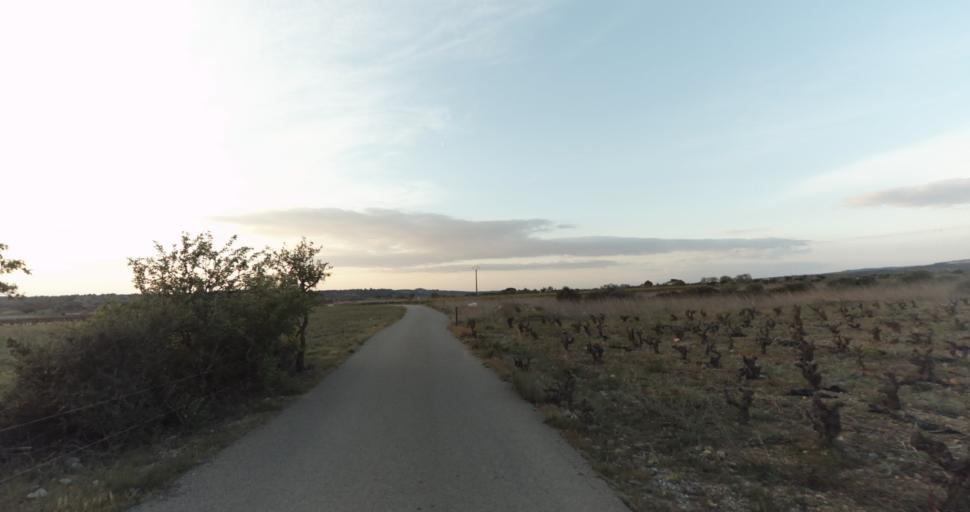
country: FR
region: Languedoc-Roussillon
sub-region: Departement de l'Aude
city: Leucate
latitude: 42.9370
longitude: 3.0002
